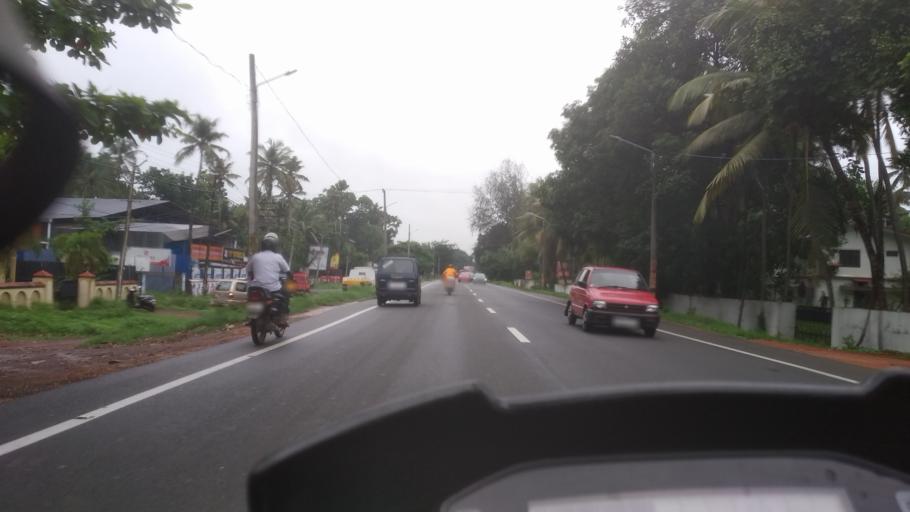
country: IN
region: Kerala
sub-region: Alappuzha
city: Kayankulam
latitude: 9.1842
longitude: 76.4903
